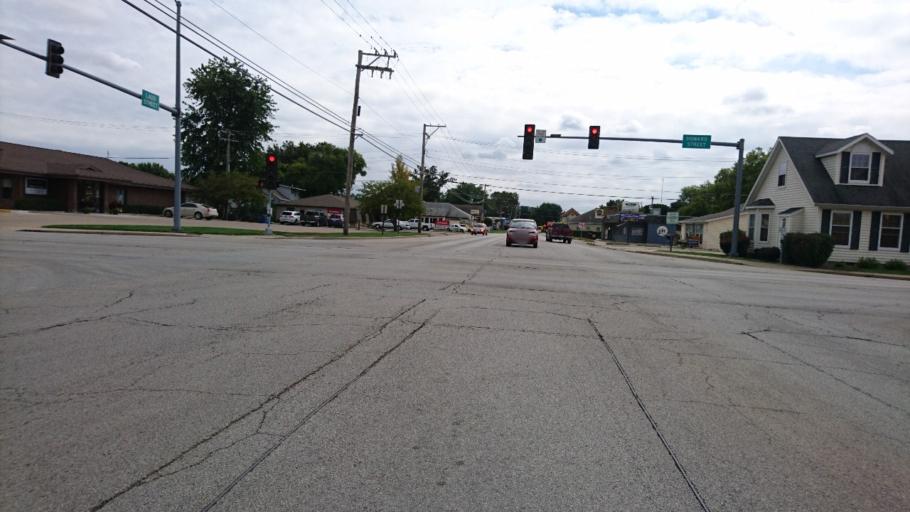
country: US
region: Illinois
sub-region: Livingston County
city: Pontiac
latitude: 40.8811
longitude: -88.6381
